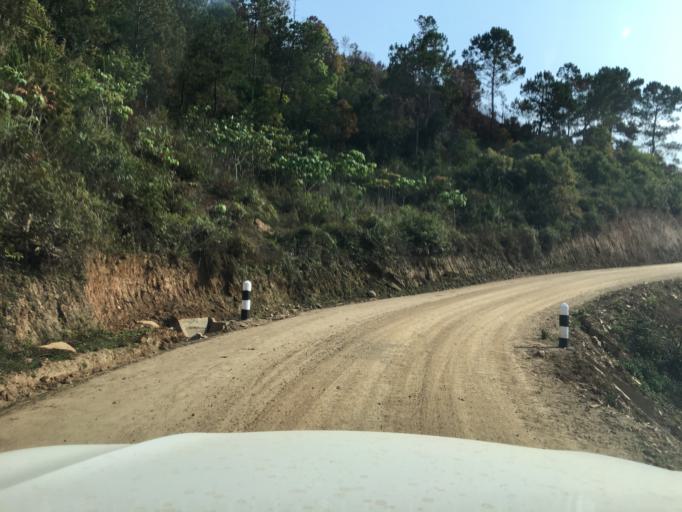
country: LA
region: Houaphan
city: Huameung
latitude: 20.2052
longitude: 103.8326
